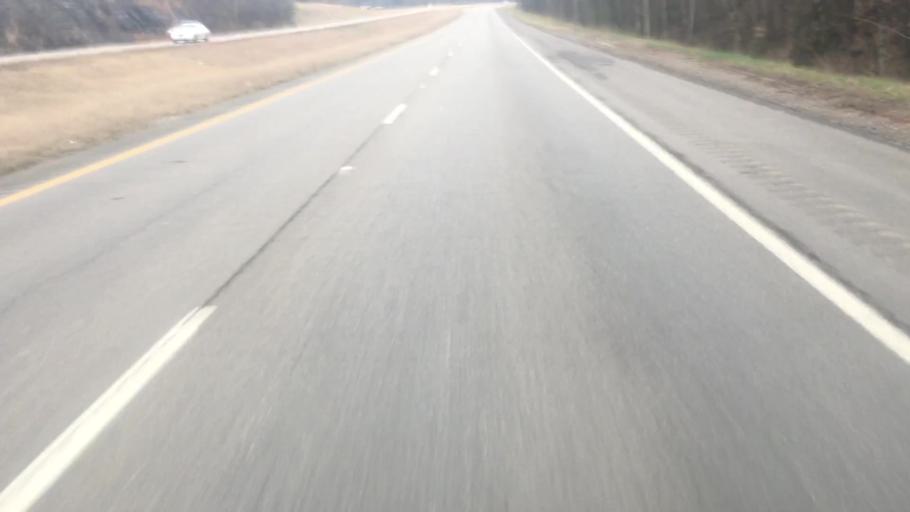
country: US
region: Alabama
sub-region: Walker County
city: Sumiton
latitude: 33.7763
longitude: -87.0790
